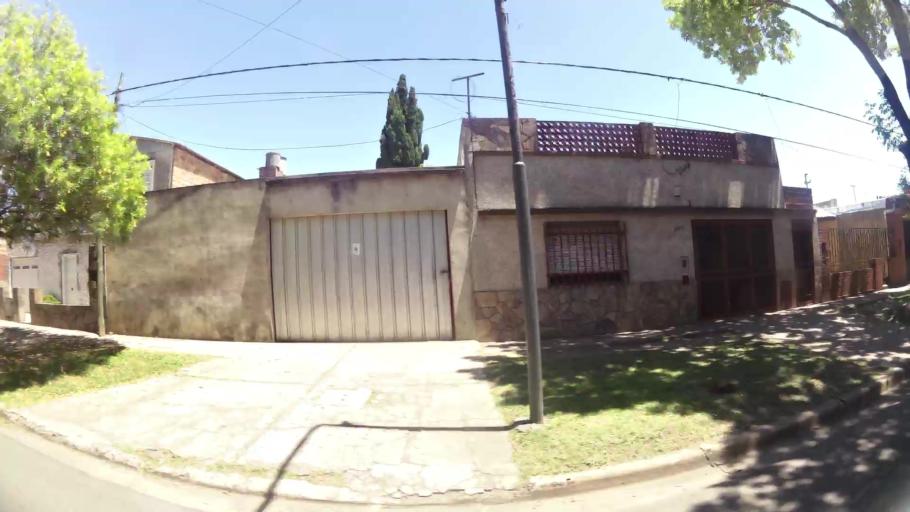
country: AR
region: Santa Fe
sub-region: Departamento de Rosario
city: Rosario
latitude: -32.9536
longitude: -60.6942
